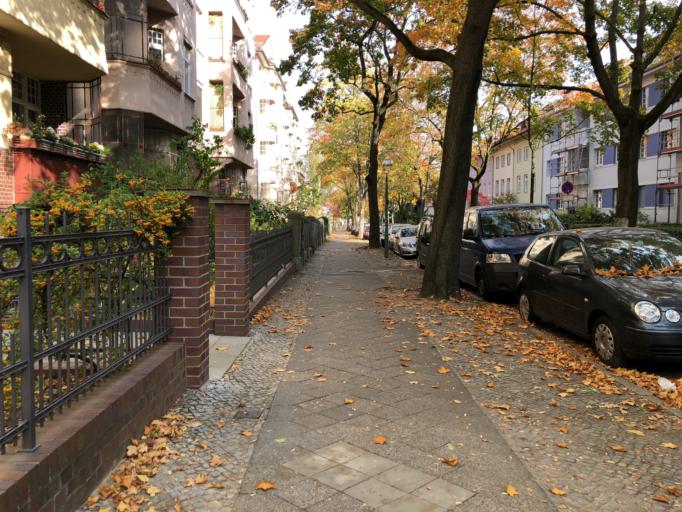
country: DE
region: Berlin
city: Lichterfelde
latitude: 52.4485
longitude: 13.3065
